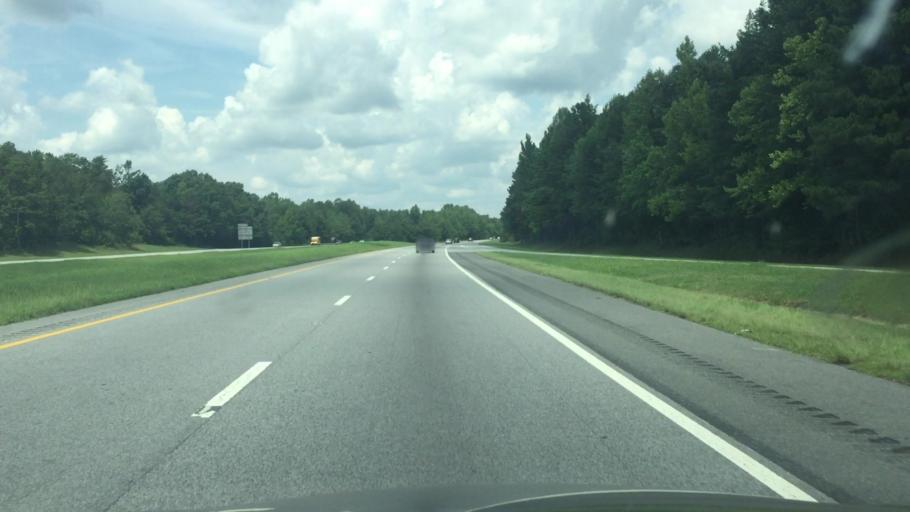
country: US
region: North Carolina
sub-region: Guilford County
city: Pleasant Garden
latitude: 35.9252
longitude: -79.8262
